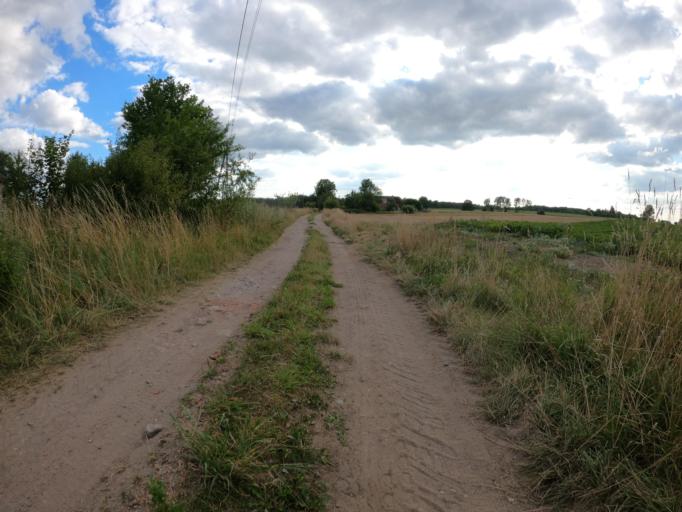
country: PL
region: West Pomeranian Voivodeship
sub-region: Powiat lobeski
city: Lobez
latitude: 53.7559
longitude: 15.6505
